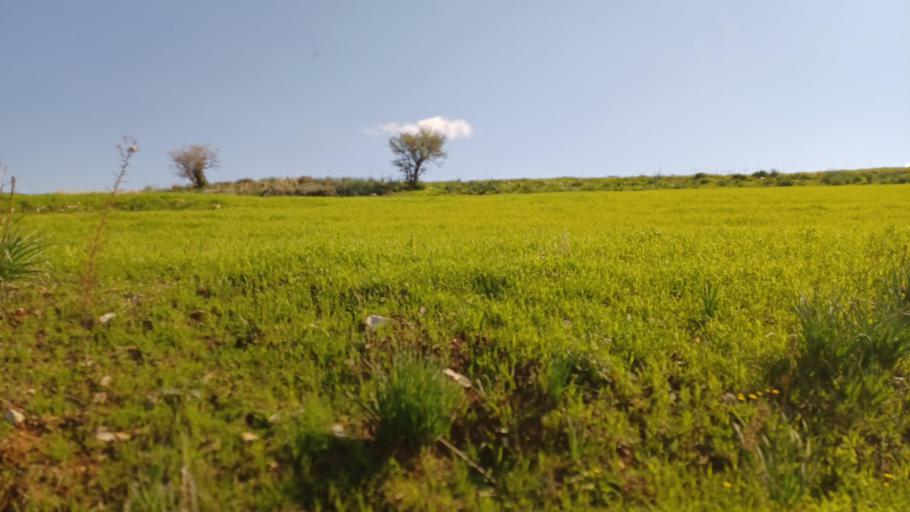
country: CY
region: Pafos
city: Mesogi
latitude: 34.7564
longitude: 32.5345
